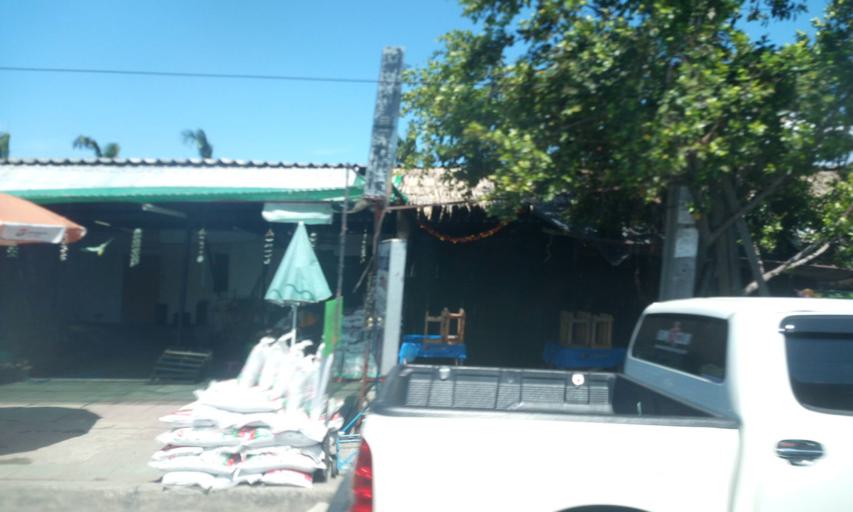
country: TH
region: Samut Prakan
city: Bang Bo District
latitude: 13.5586
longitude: 100.7892
